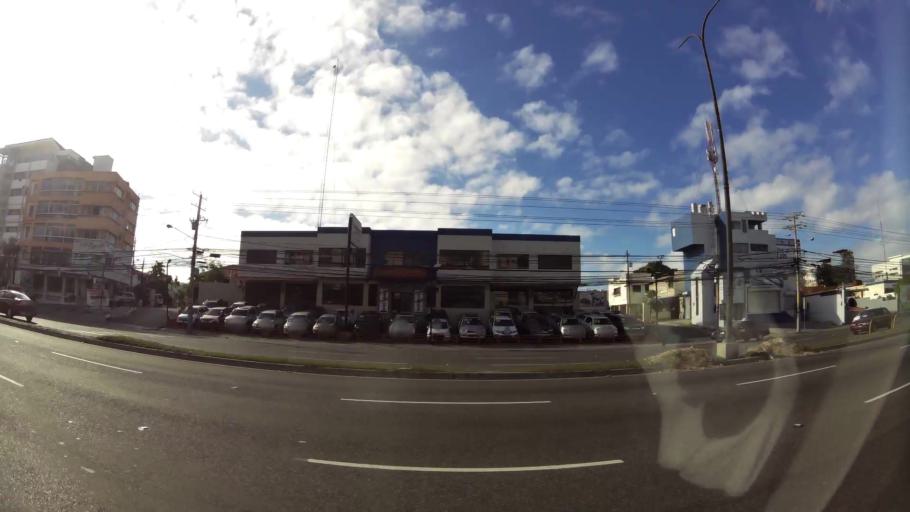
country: DO
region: Nacional
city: Bella Vista
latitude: 18.4593
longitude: -69.9434
